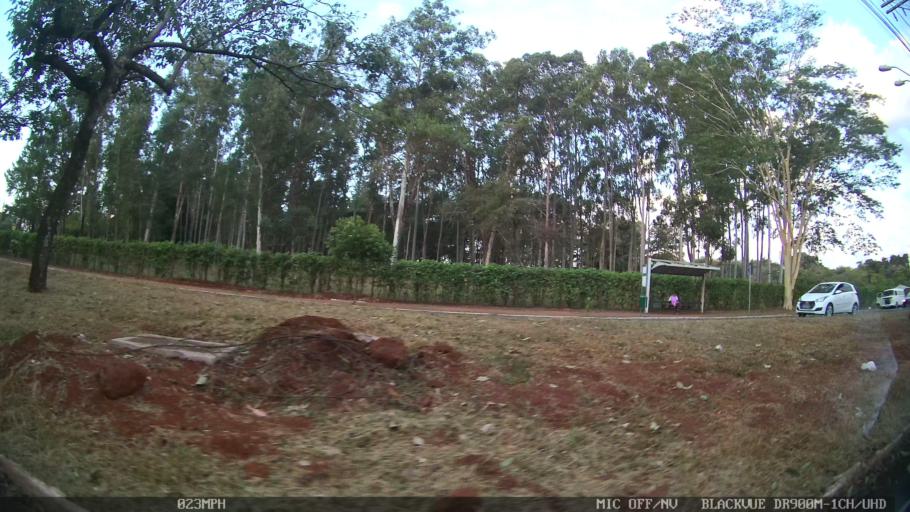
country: BR
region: Sao Paulo
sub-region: Ribeirao Preto
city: Ribeirao Preto
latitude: -21.1649
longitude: -47.7898
